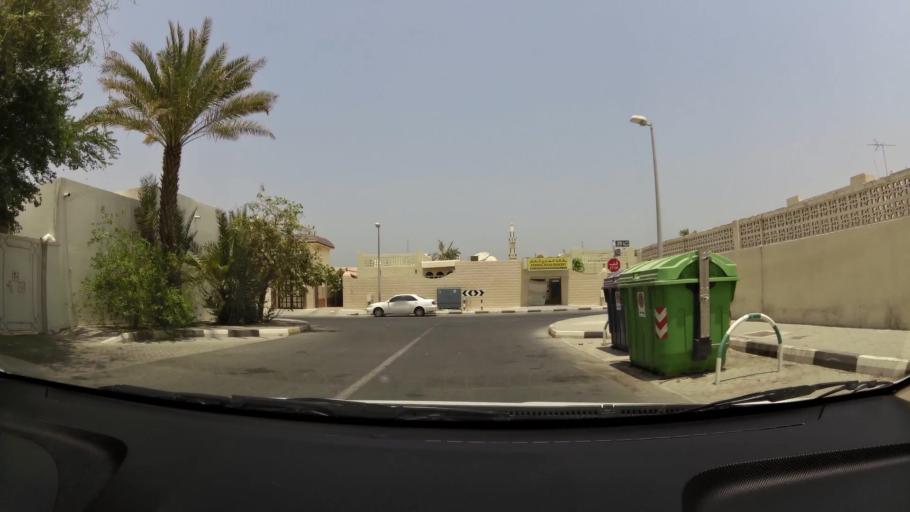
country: AE
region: Ash Shariqah
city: Sharjah
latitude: 25.3408
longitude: 55.3698
